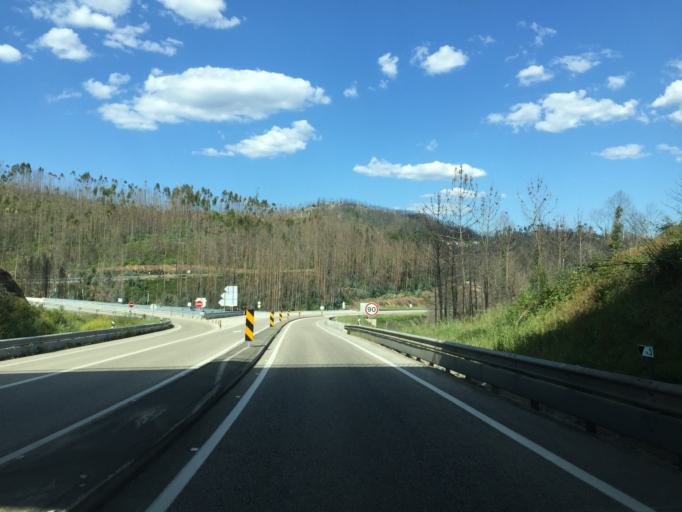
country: PT
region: Leiria
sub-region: Figueiro Dos Vinhos
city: Figueiro dos Vinhos
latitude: 39.9267
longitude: -8.3291
